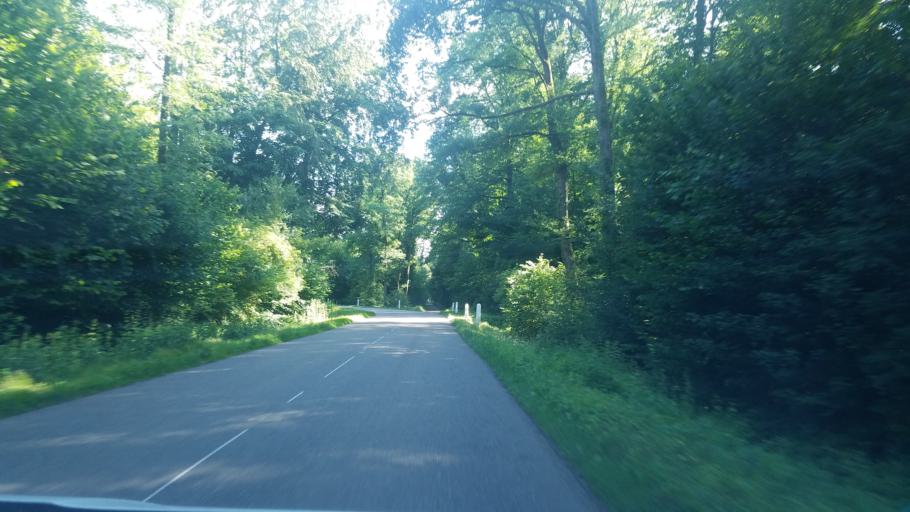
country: FR
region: Alsace
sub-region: Departement du Bas-Rhin
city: Drusenheim
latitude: 48.7944
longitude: 7.9517
